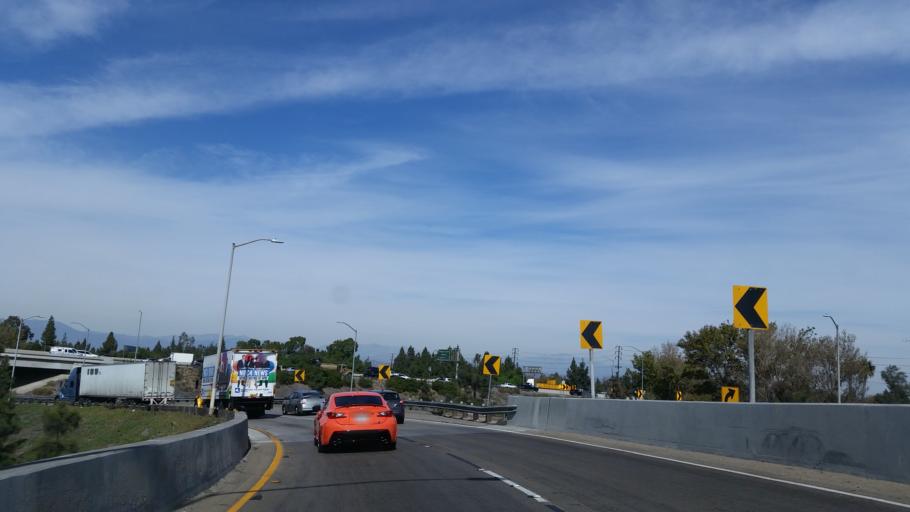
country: US
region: California
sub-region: Los Angeles County
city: Bellflower
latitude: 33.8746
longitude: -118.1020
